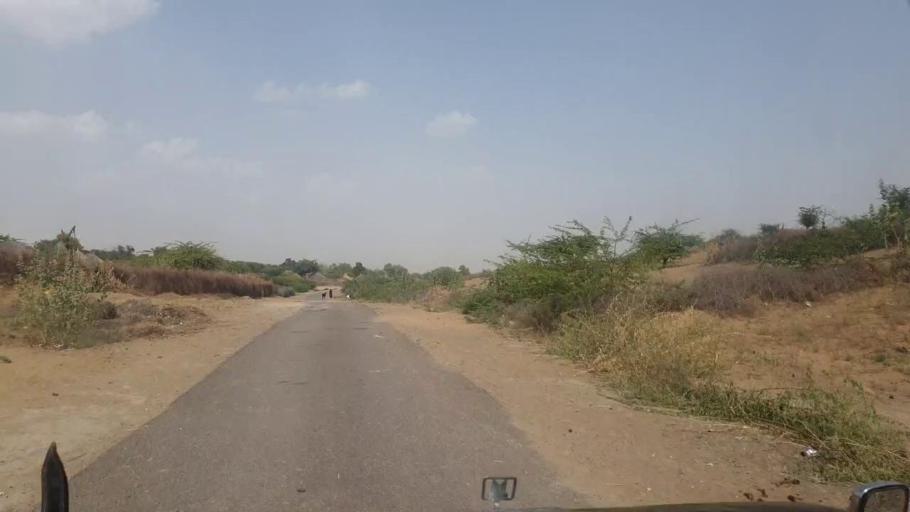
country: PK
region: Sindh
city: Islamkot
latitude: 25.2327
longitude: 70.2850
